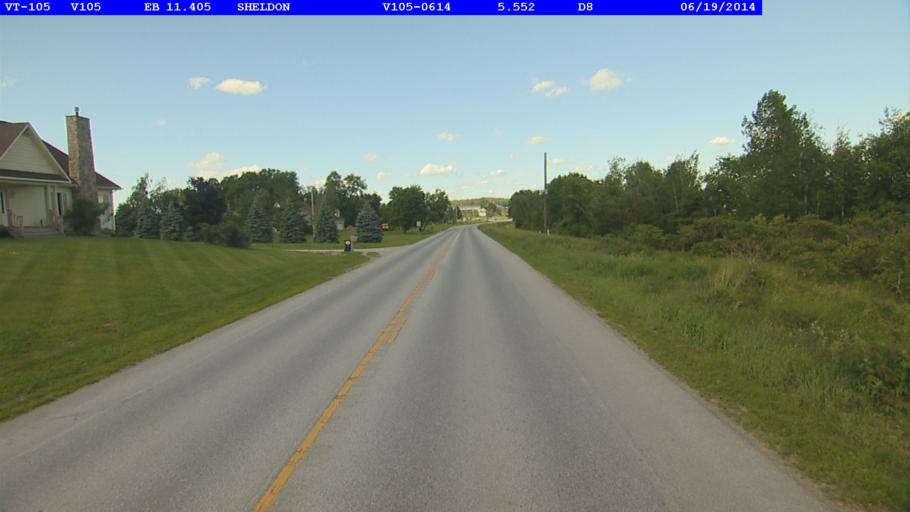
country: US
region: Vermont
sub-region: Franklin County
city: Enosburg Falls
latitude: 44.9047
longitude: -72.9260
